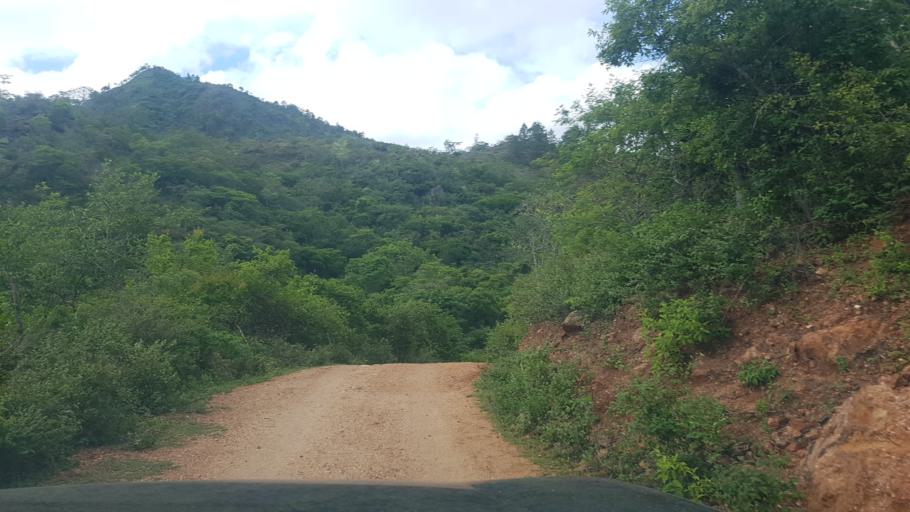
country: NI
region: Nueva Segovia
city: Ocotal
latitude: 13.6357
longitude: -86.6040
